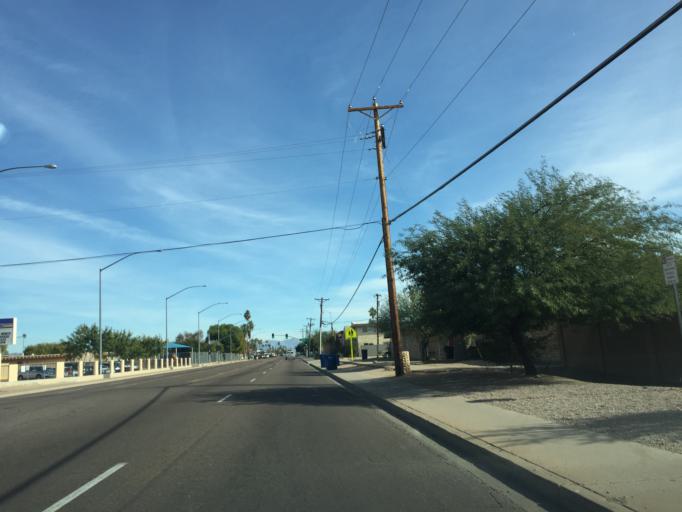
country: US
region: Arizona
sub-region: Maricopa County
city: Mesa
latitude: 33.4080
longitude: -111.7936
